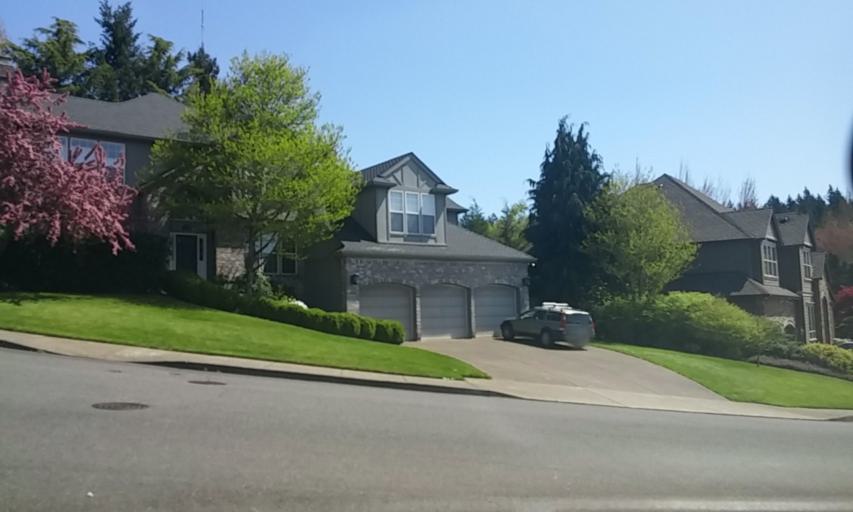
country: US
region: Oregon
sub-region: Washington County
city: West Haven
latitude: 45.5256
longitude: -122.7640
